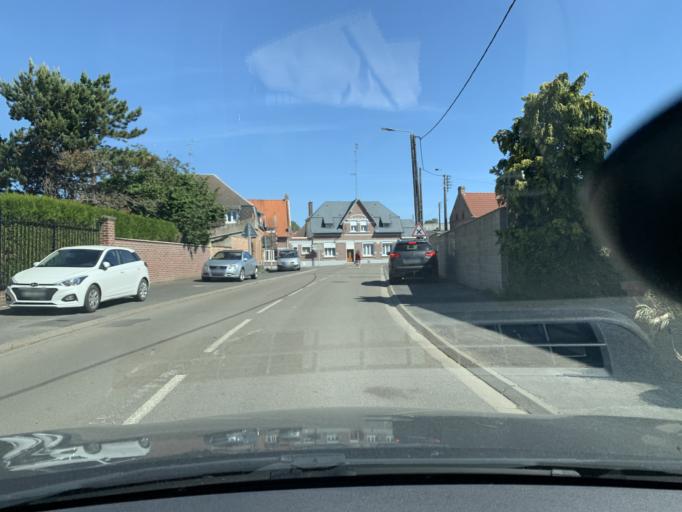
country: FR
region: Nord-Pas-de-Calais
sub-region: Departement du Nord
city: Fontaine-Notre-Dame
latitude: 50.1653
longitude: 3.1562
